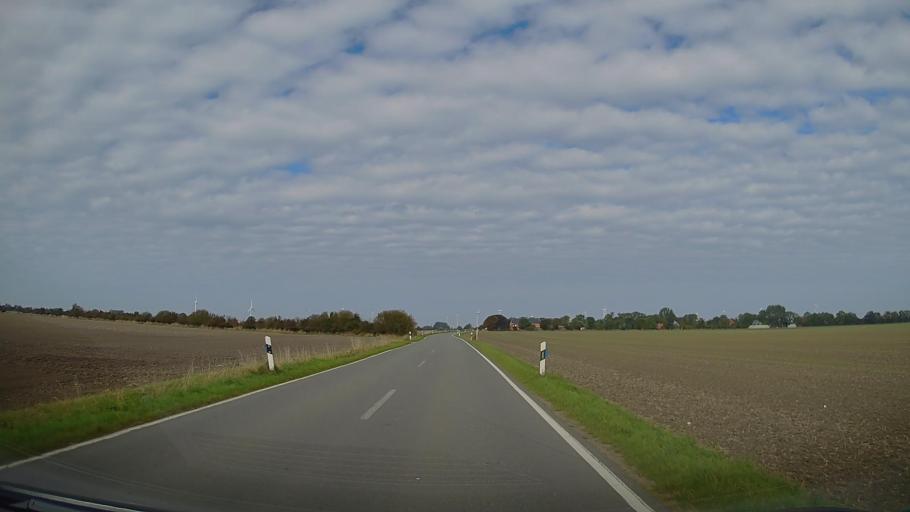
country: DE
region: Schleswig-Holstein
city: Grossenbrode
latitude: 54.4900
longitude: 11.0617
